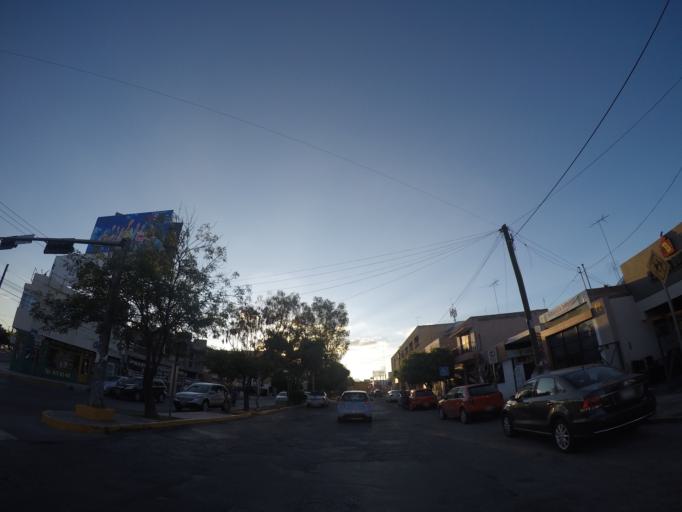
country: MX
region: San Luis Potosi
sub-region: San Luis Potosi
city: San Luis Potosi
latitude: 22.1428
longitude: -100.9996
